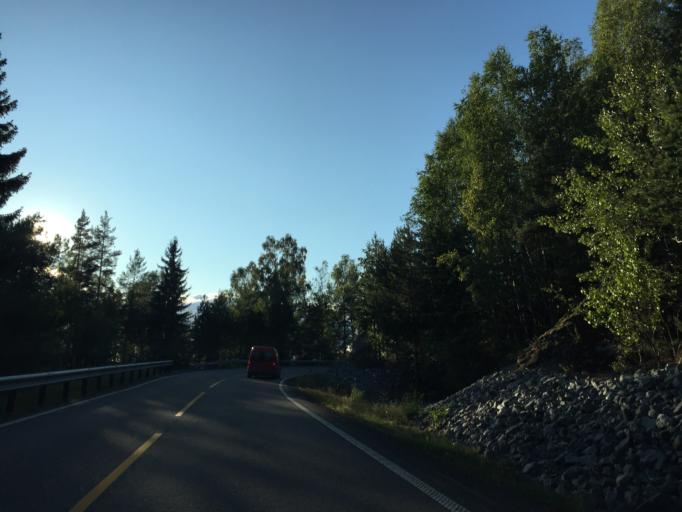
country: NO
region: Akershus
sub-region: Enebakk
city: Flateby
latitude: 59.8182
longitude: 11.2447
